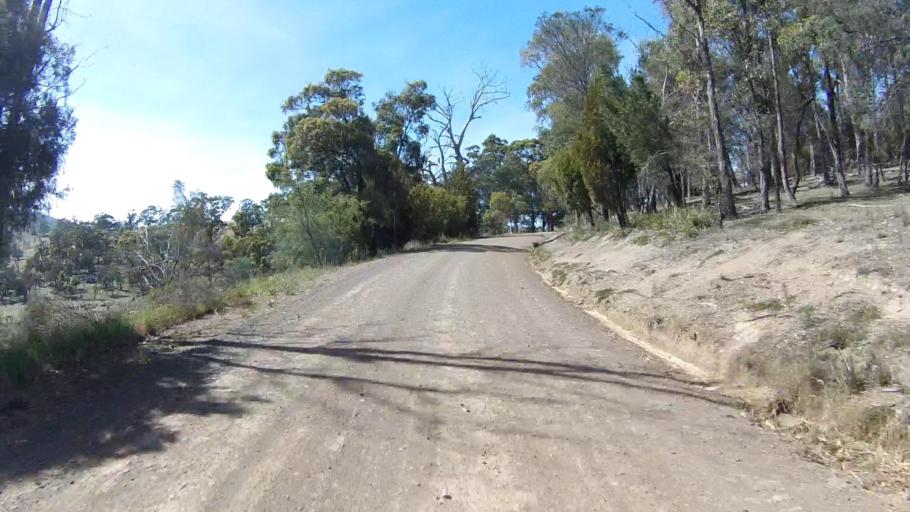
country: AU
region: Tasmania
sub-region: Sorell
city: Sorell
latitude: -42.7367
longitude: 147.5975
